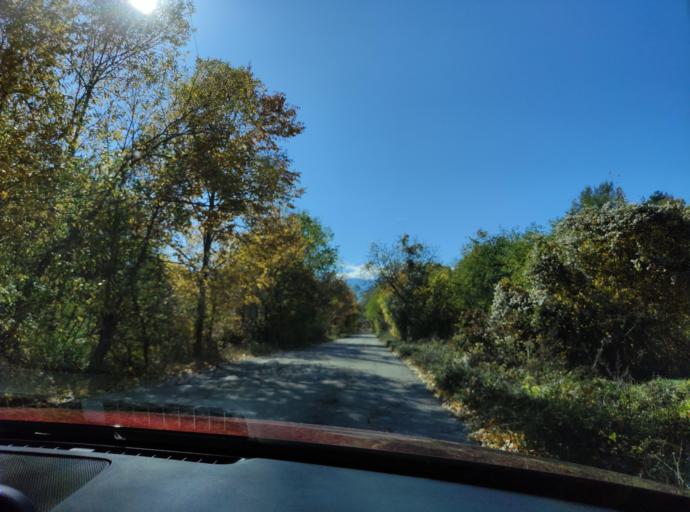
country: BG
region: Montana
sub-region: Obshtina Chiprovtsi
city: Chiprovtsi
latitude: 43.4028
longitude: 22.9356
